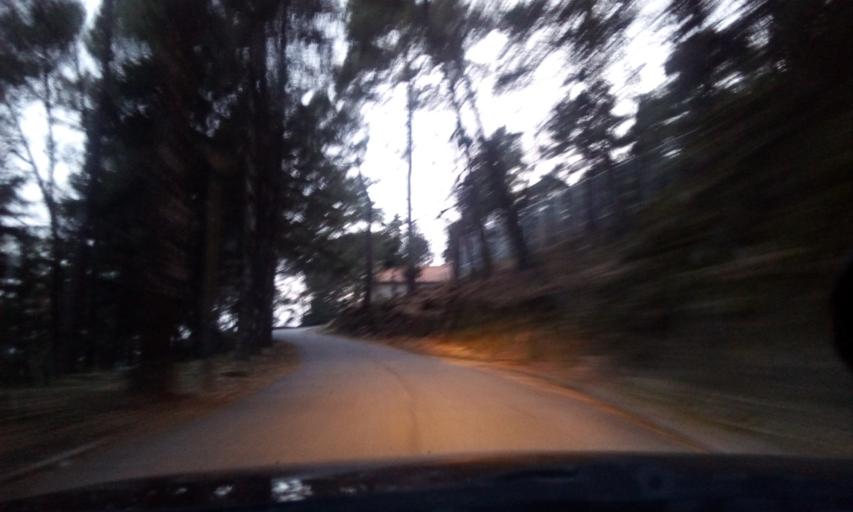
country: PT
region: Guarda
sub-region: Fornos de Algodres
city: Fornos de Algodres
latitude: 40.6214
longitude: -7.5433
